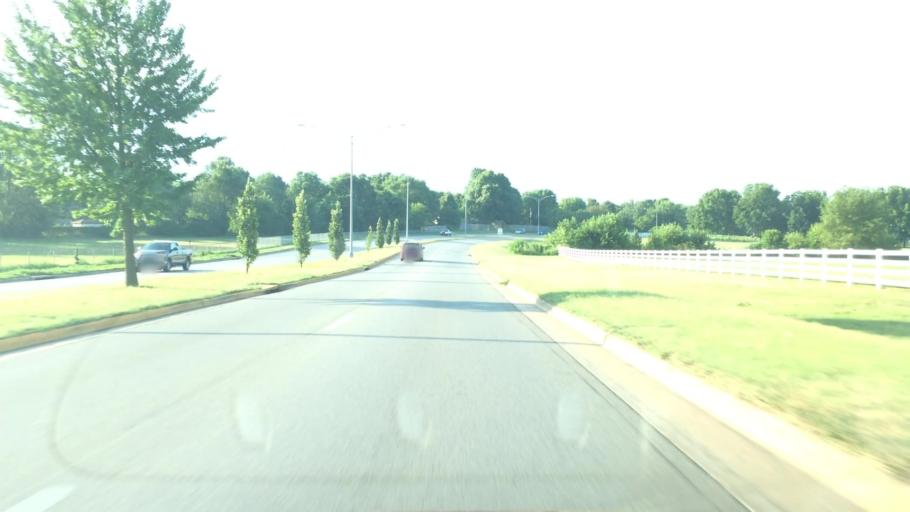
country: US
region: Missouri
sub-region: Greene County
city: Springfield
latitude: 37.1751
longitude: -93.3175
